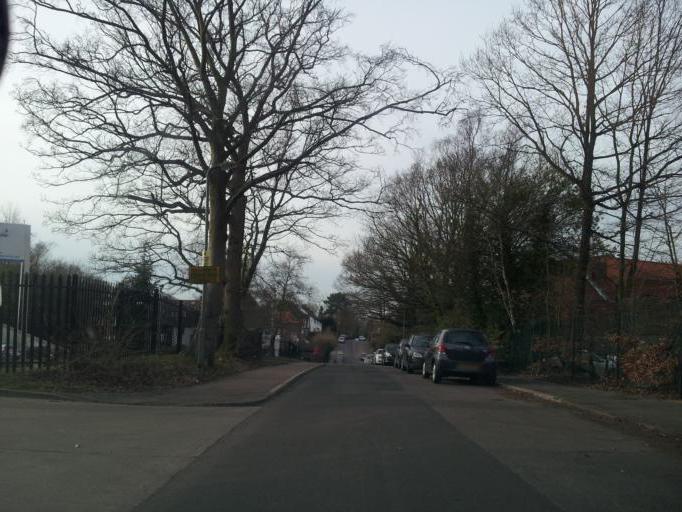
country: GB
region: England
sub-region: Greater London
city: Stanmore
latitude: 51.6367
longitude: -0.3319
